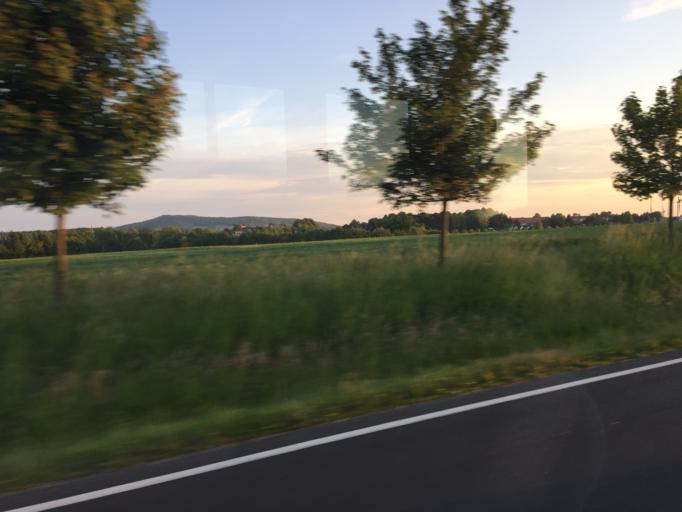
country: DE
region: Saxony
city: Reichenbach
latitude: 51.1489
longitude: 14.8052
